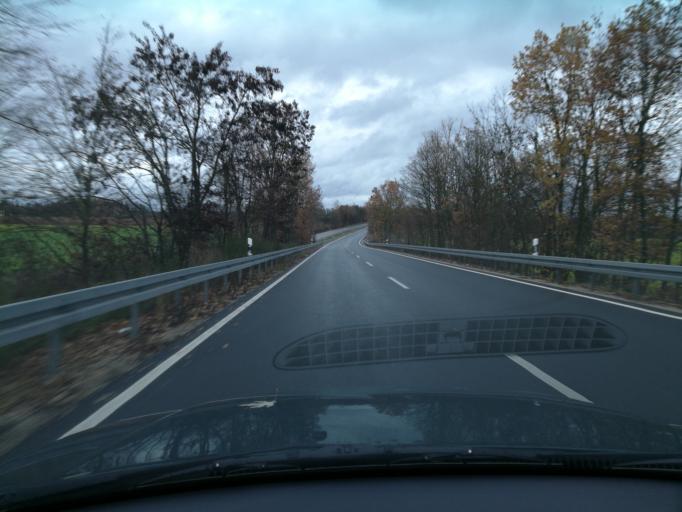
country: DE
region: Bavaria
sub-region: Regierungsbezirk Mittelfranken
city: Zirndorf
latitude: 49.4789
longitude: 10.9308
